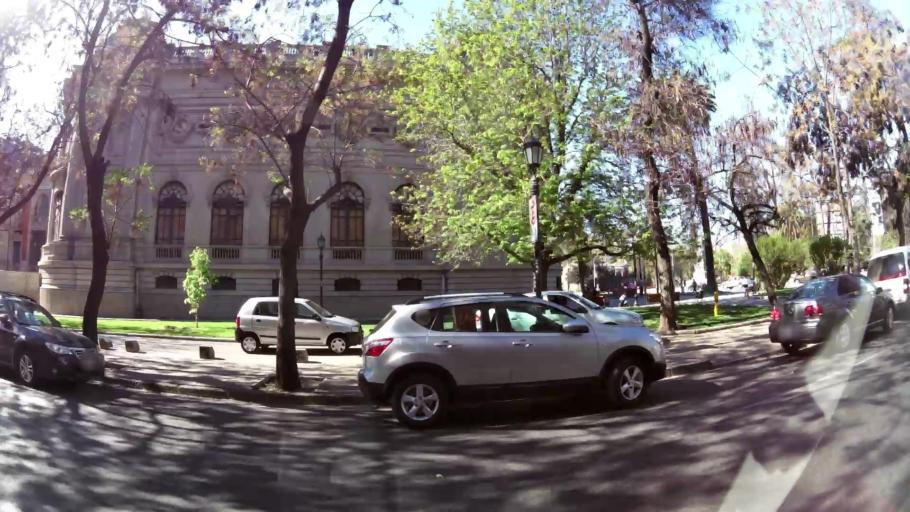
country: CL
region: Santiago Metropolitan
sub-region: Provincia de Santiago
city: Santiago
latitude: -33.4358
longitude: -70.6437
